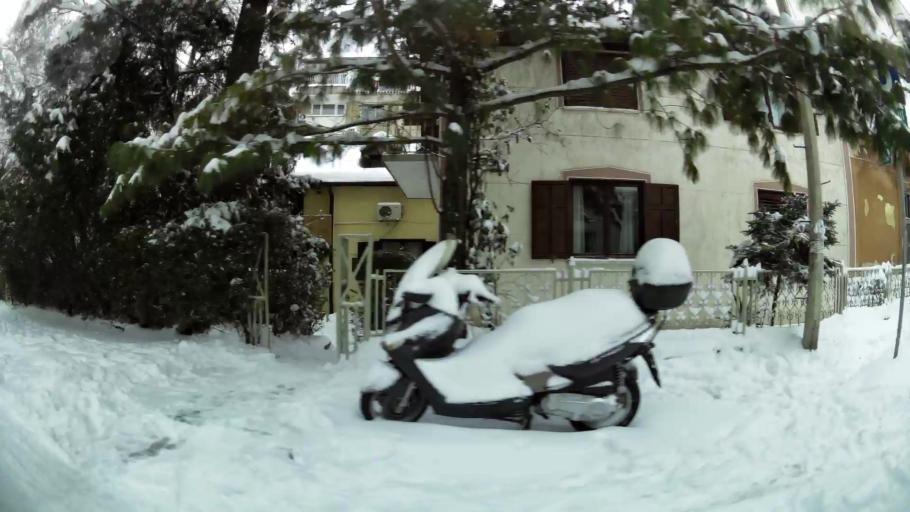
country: RS
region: Central Serbia
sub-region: Belgrade
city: Vracar
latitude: 44.7966
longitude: 20.4811
